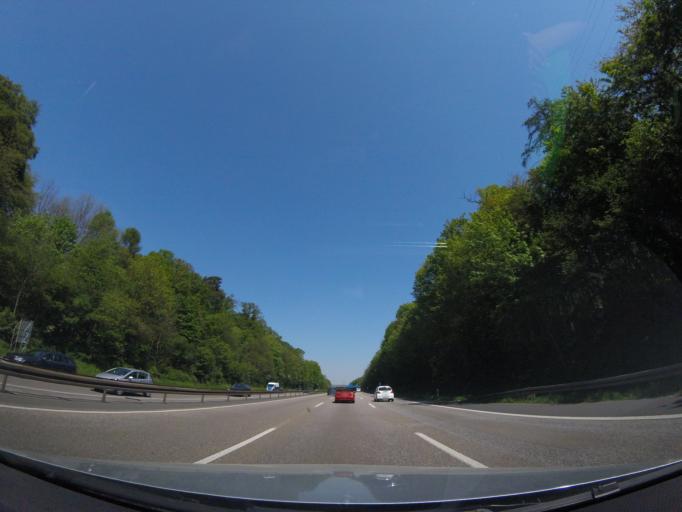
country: DE
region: Hesse
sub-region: Regierungsbezirk Darmstadt
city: Offenbach
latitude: 50.0877
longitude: 8.7379
